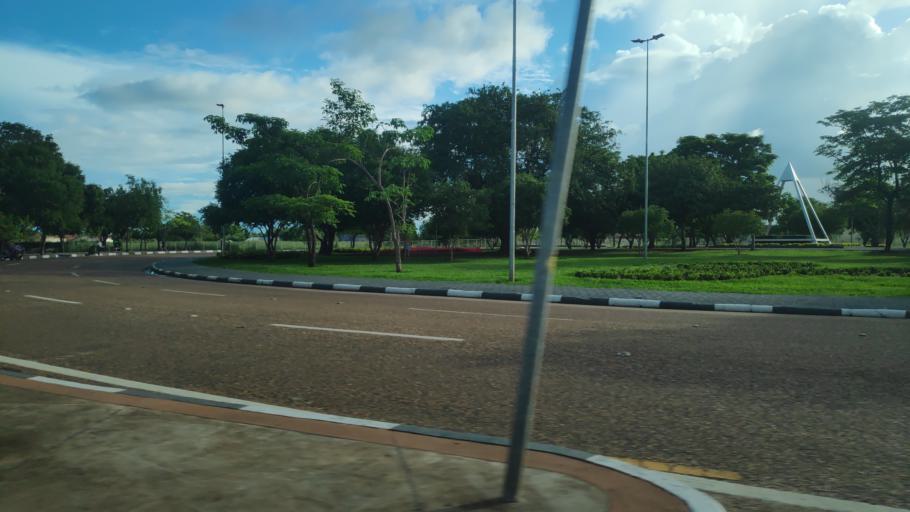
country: BR
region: Roraima
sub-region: Boa Vista
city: Boa Vista
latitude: 2.8362
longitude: -60.6893
